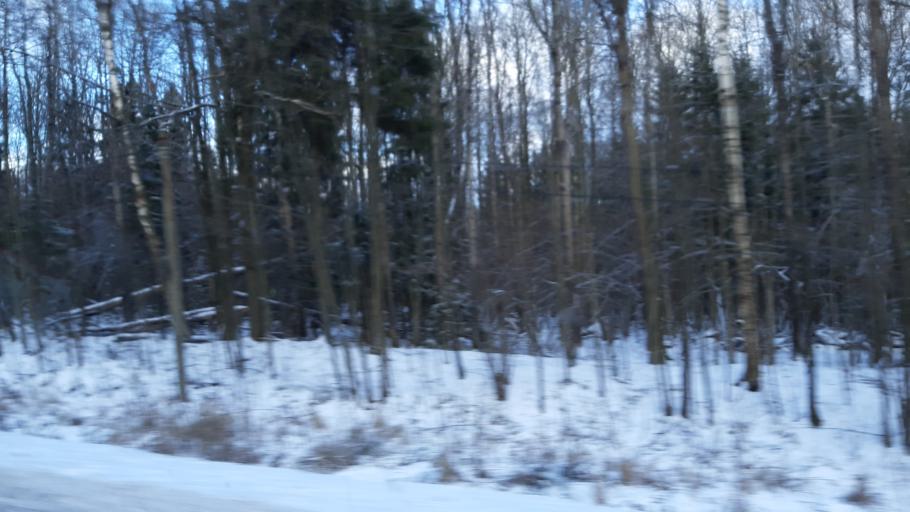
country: RU
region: Moskovskaya
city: Svatkovo
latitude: 56.3172
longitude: 38.3028
